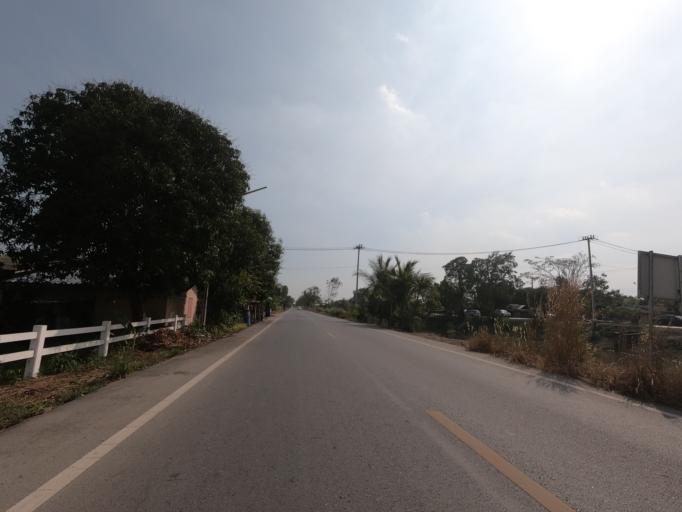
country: TH
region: Pathum Thani
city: Nong Suea
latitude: 14.0798
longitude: 100.8467
